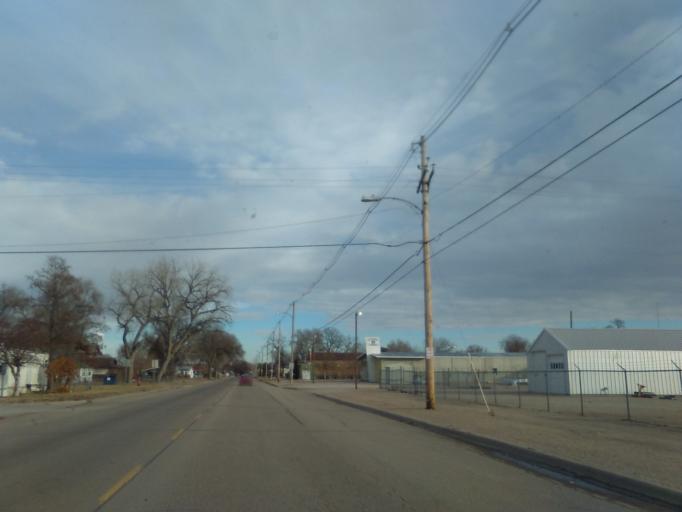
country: US
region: Nebraska
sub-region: Morrill County
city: Bridgeport
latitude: 41.6704
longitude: -103.1055
